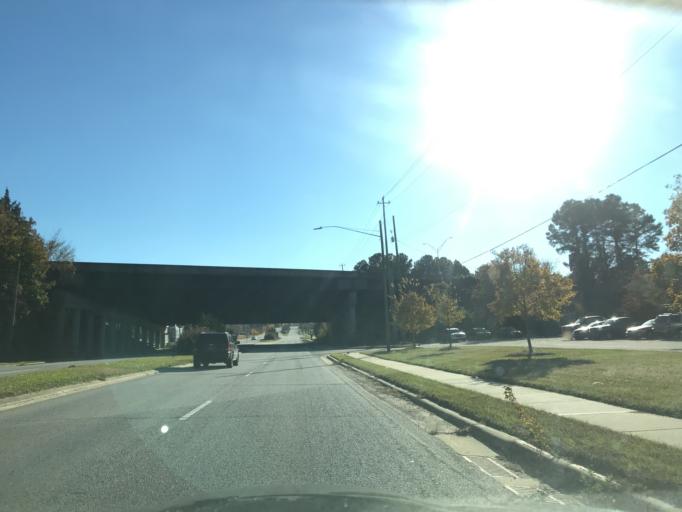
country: US
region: North Carolina
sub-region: Wake County
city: Raleigh
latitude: 35.7556
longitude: -78.6412
